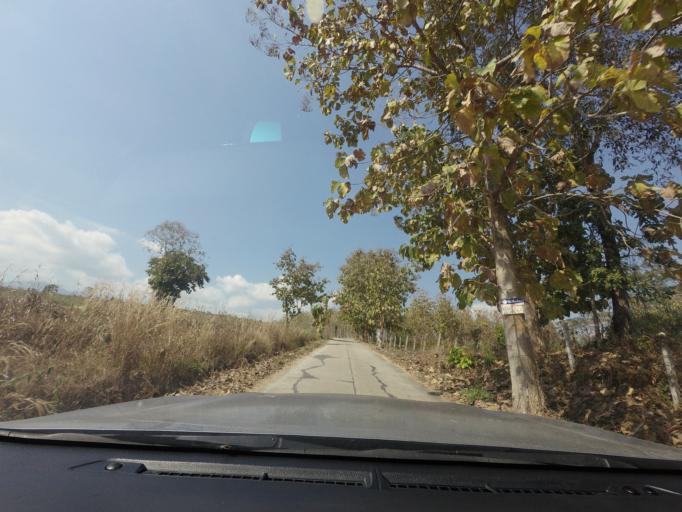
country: TH
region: Mae Hong Son
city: Wiang Nuea
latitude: 19.3837
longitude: 98.4363
